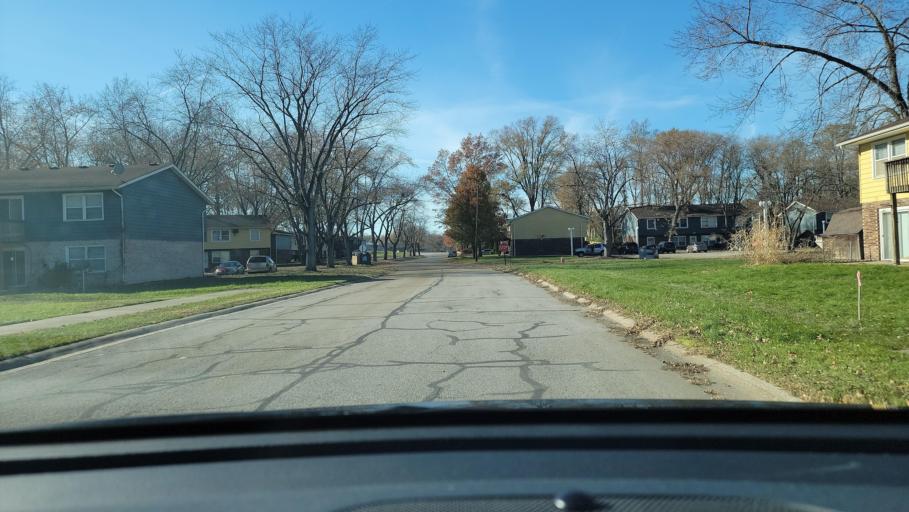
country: US
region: Indiana
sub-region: Porter County
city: Portage
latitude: 41.5823
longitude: -87.1806
